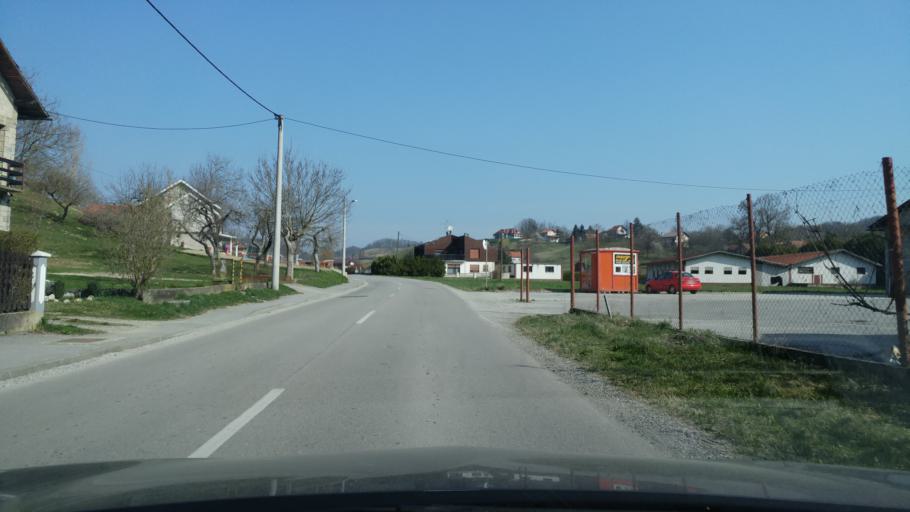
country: HR
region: Zagrebacka
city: Pojatno
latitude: 45.9224
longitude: 15.7726
